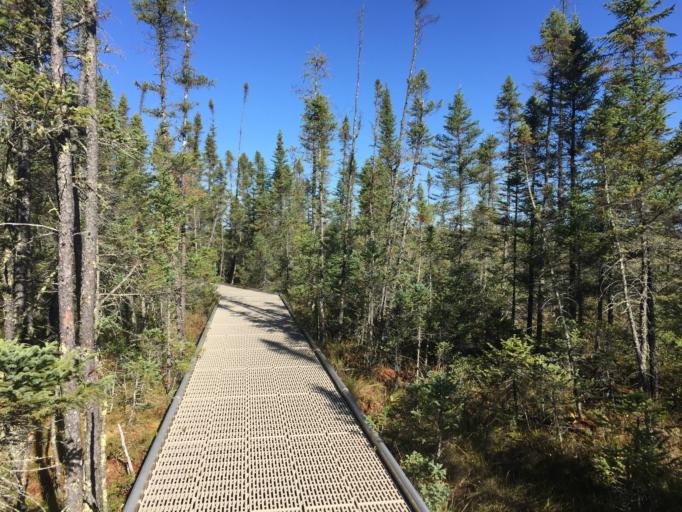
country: US
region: Minnesota
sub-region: Lake of the Woods County
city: Baudette
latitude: 48.2992
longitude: -94.5680
